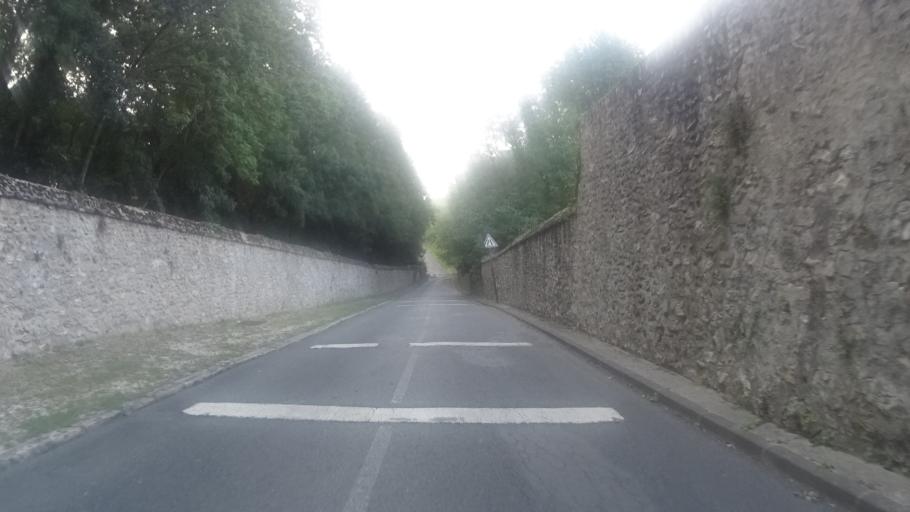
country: FR
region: Ile-de-France
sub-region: Departement de l'Essonne
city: Mennecy
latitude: 48.5704
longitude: 2.4114
